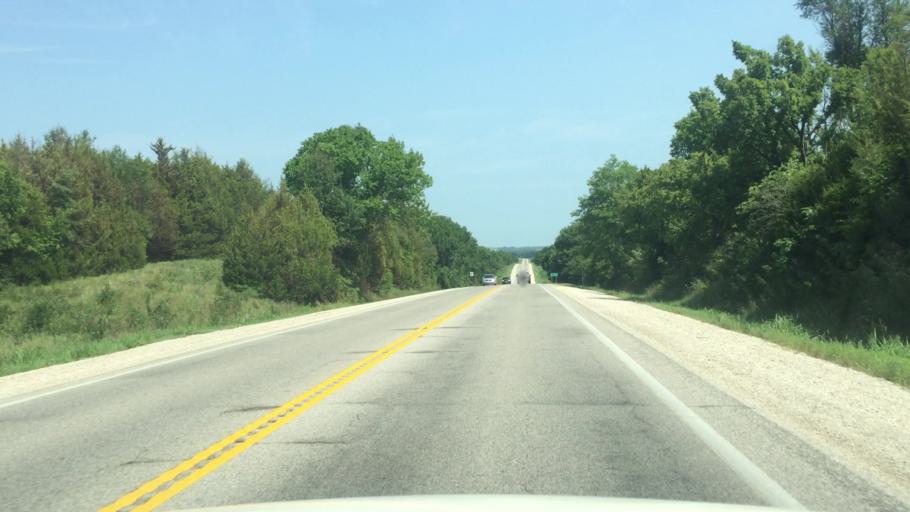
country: US
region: Kansas
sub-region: Montgomery County
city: Coffeyville
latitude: 37.1509
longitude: -95.5769
